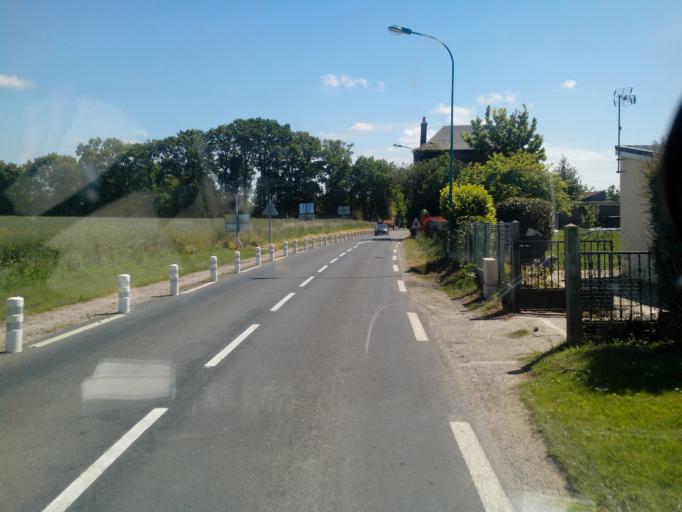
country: FR
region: Haute-Normandie
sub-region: Departement de la Seine-Maritime
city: Gonneville-la-Mallet
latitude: 49.6406
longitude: 0.2681
